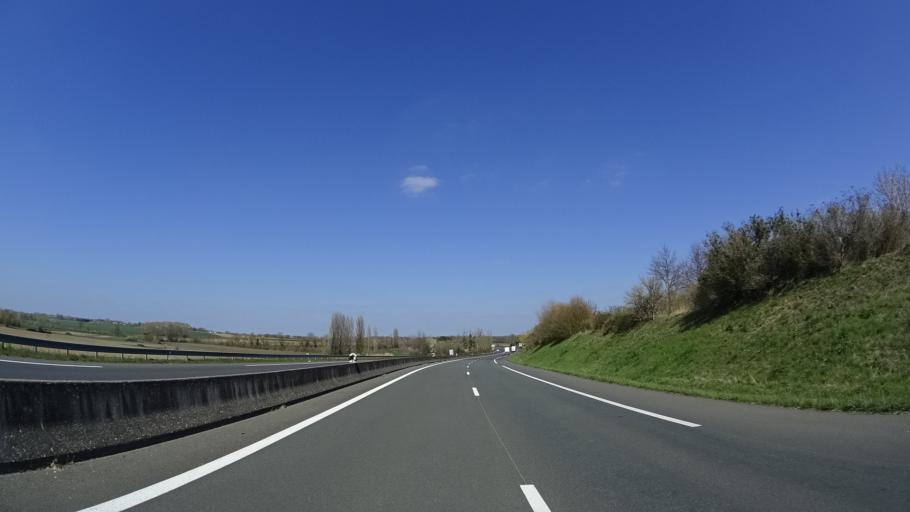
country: FR
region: Pays de la Loire
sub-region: Departement de Maine-et-Loire
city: Doue-la-Fontaine
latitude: 47.2383
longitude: -0.3206
